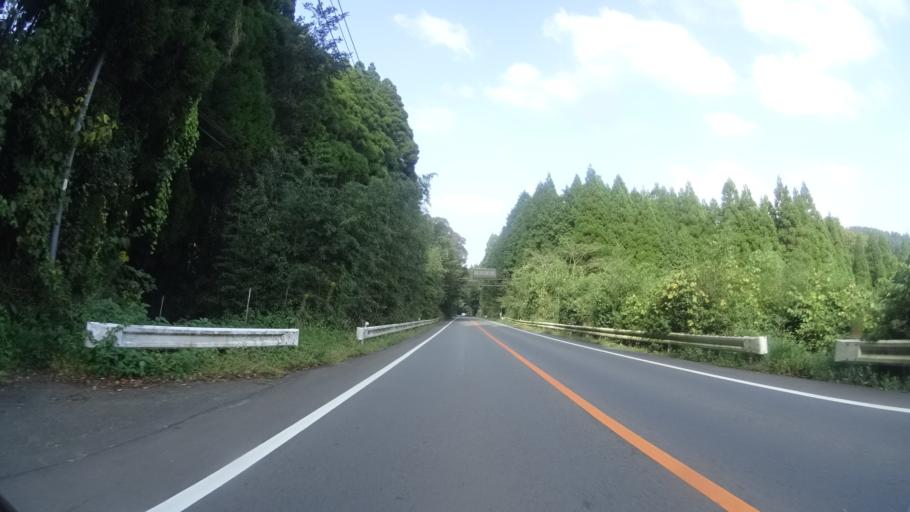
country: JP
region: Kumamoto
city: Aso
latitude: 33.0853
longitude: 131.0663
